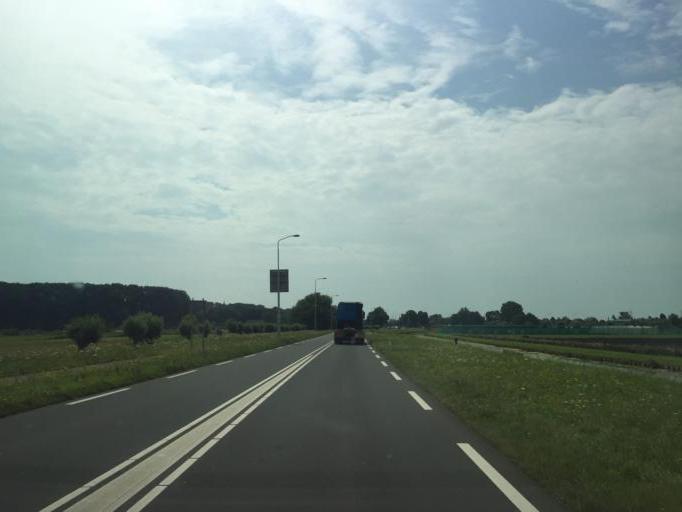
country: NL
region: North Holland
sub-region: Gemeente Enkhuizen
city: Enkhuizen
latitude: 52.7058
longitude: 5.2741
